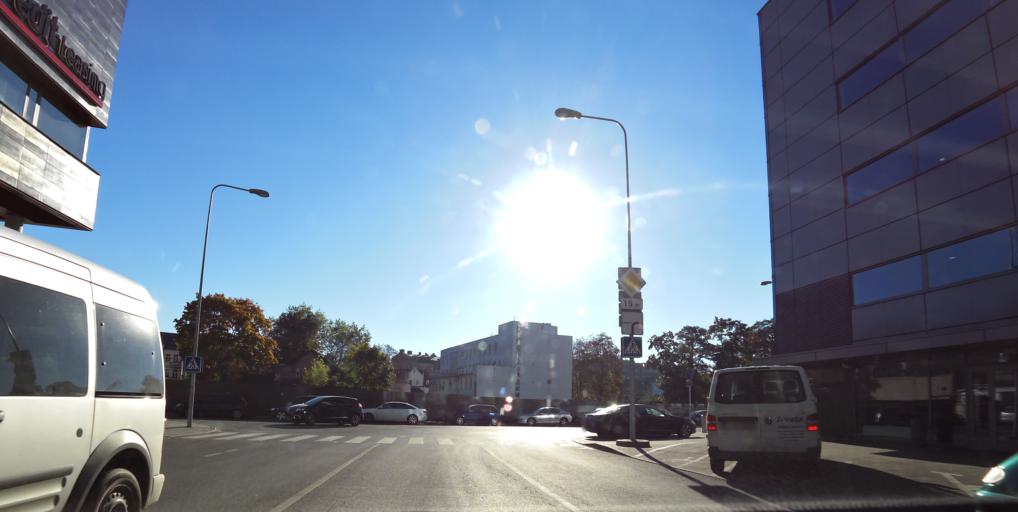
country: LT
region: Vilnius County
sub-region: Vilnius
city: Vilnius
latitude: 54.6963
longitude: 25.2793
